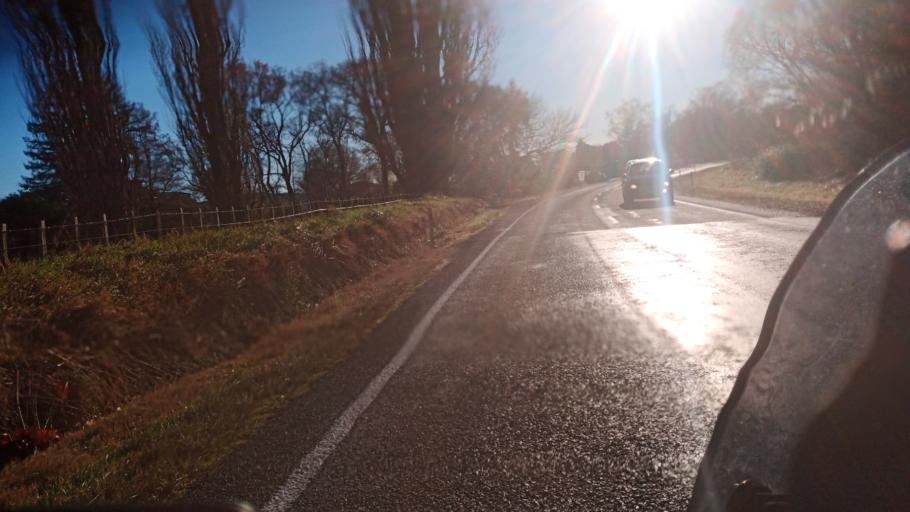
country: NZ
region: Hawke's Bay
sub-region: Wairoa District
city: Wairoa
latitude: -39.0300
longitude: 177.3692
